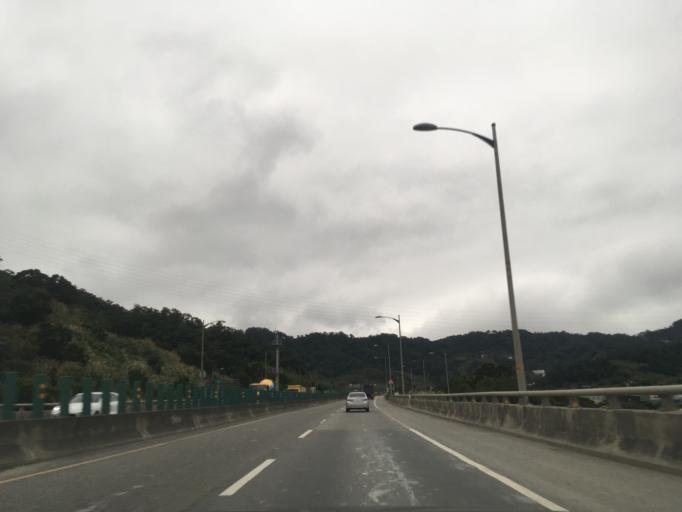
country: TW
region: Taipei
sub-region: Taipei
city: Banqiao
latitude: 25.1091
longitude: 121.4283
